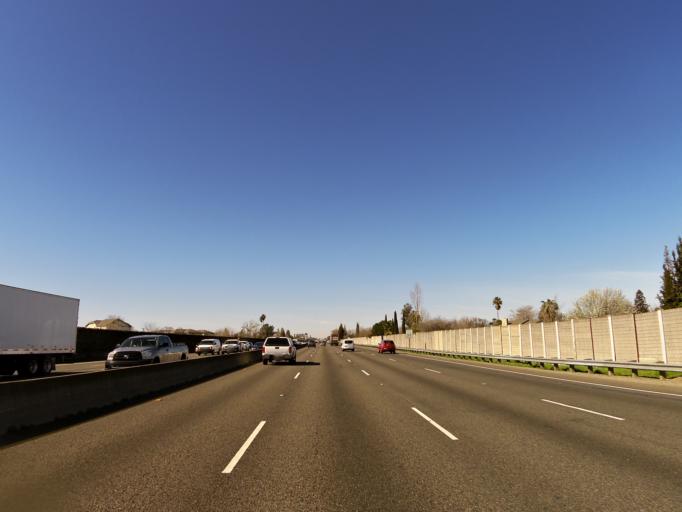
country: US
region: California
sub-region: Sacramento County
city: Florin
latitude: 38.4815
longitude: -121.4293
